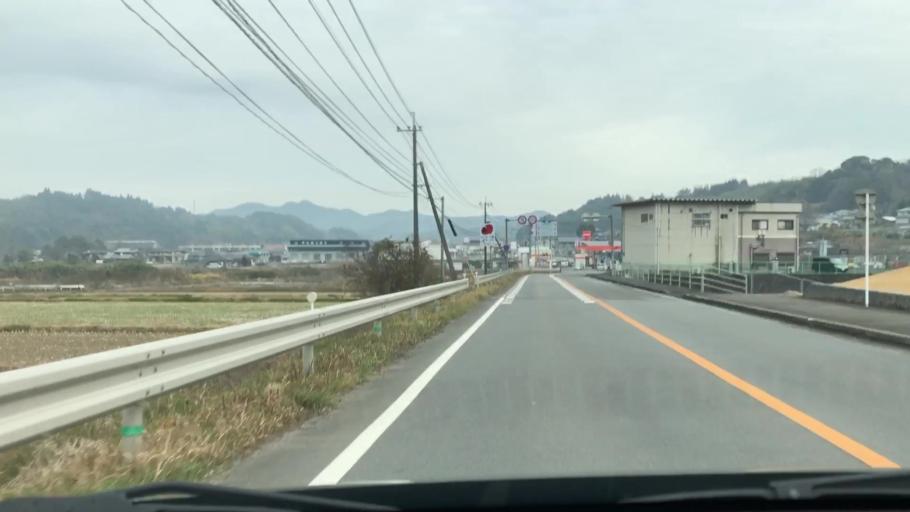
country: JP
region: Oita
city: Usuki
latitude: 33.0314
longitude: 131.6883
